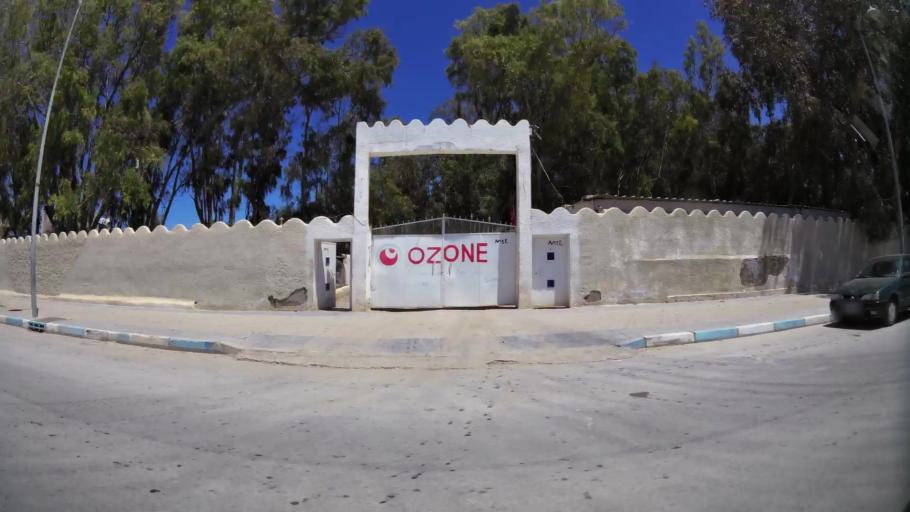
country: MA
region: Oriental
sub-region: Berkane-Taourirt
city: Madagh
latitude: 35.0829
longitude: -2.2199
